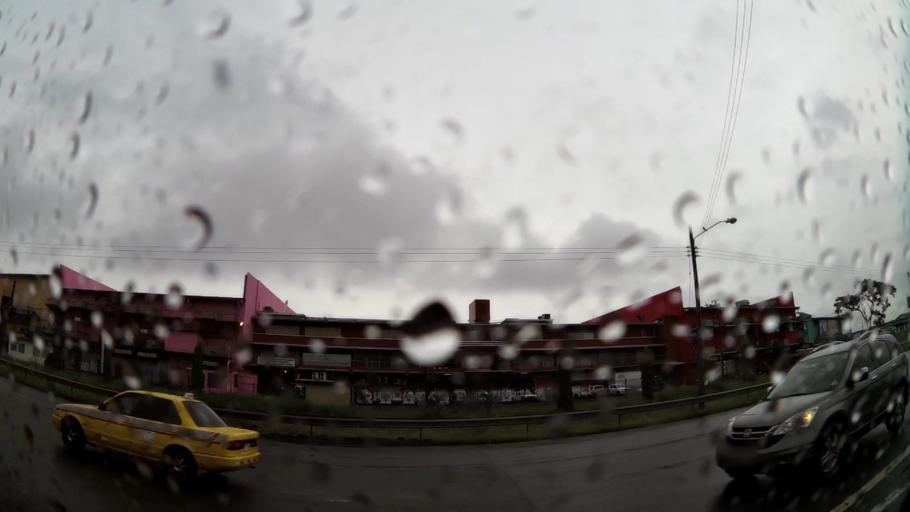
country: PA
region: Colon
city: Arco Iris
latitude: 9.3374
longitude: -79.8829
